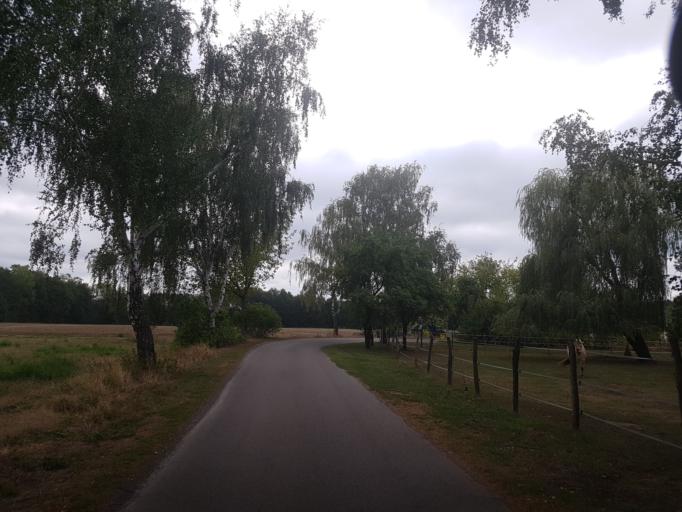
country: DE
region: Brandenburg
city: Calau
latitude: 51.7279
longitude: 13.9612
